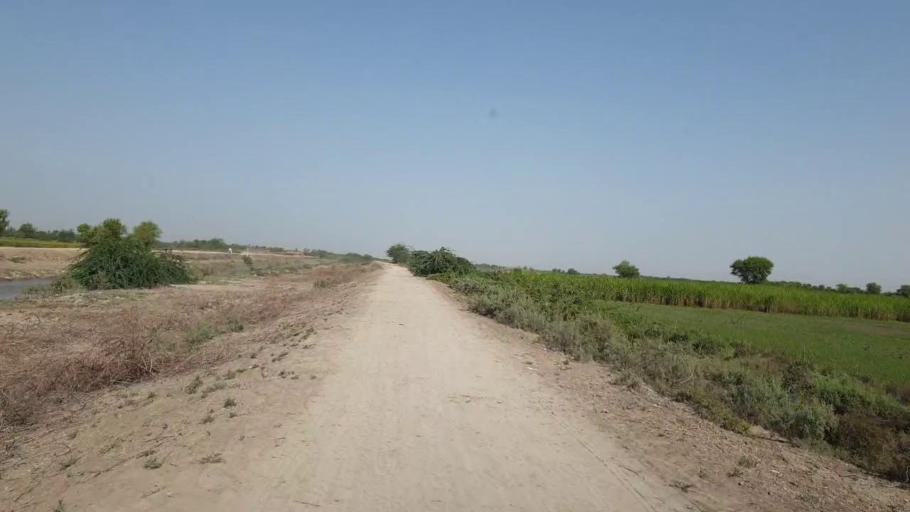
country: PK
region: Sindh
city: Kadhan
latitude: 24.6398
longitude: 69.0725
